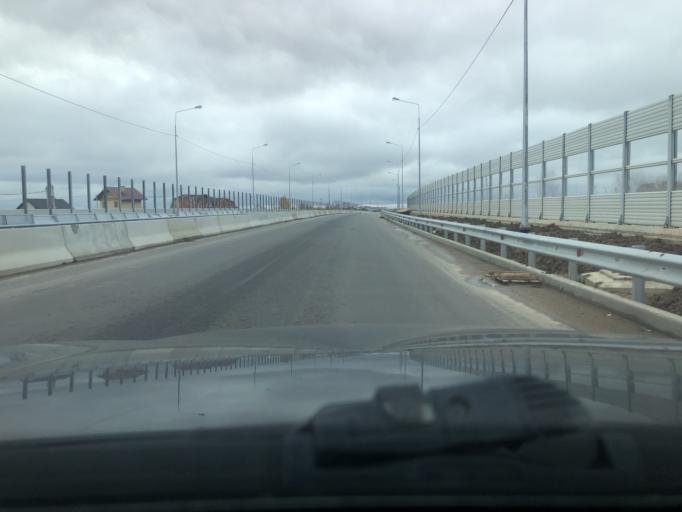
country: RU
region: Moskovskaya
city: Semkhoz
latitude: 56.3137
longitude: 38.0940
